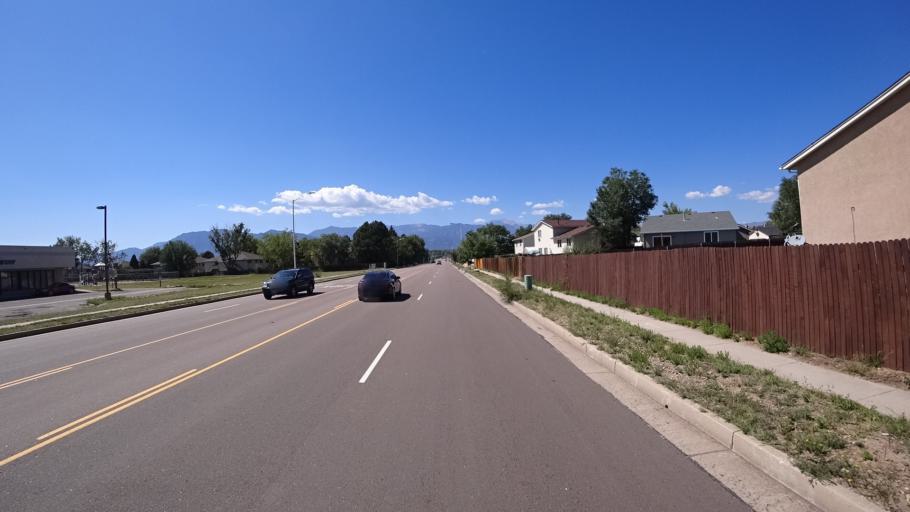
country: US
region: Colorado
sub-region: El Paso County
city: Stratmoor
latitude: 38.8050
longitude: -104.7474
